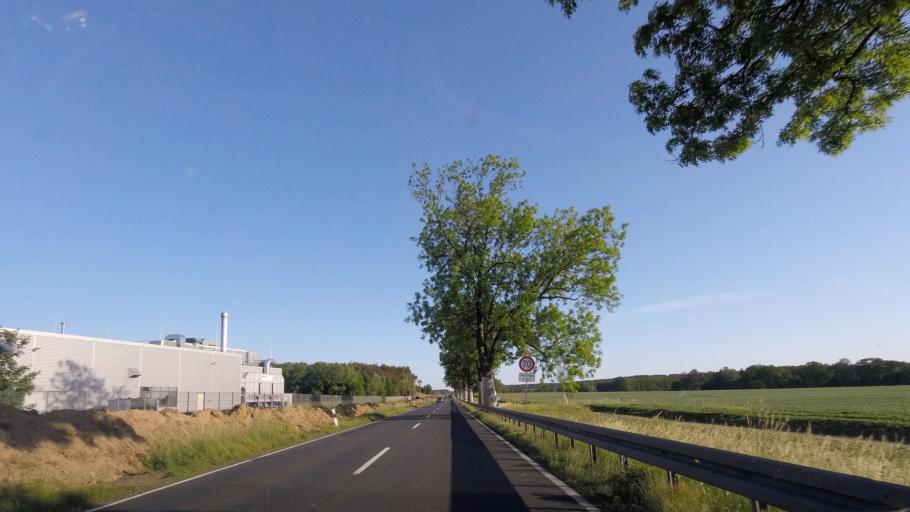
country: DE
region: Brandenburg
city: Brandenburg an der Havel
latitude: 52.3767
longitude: 12.5943
